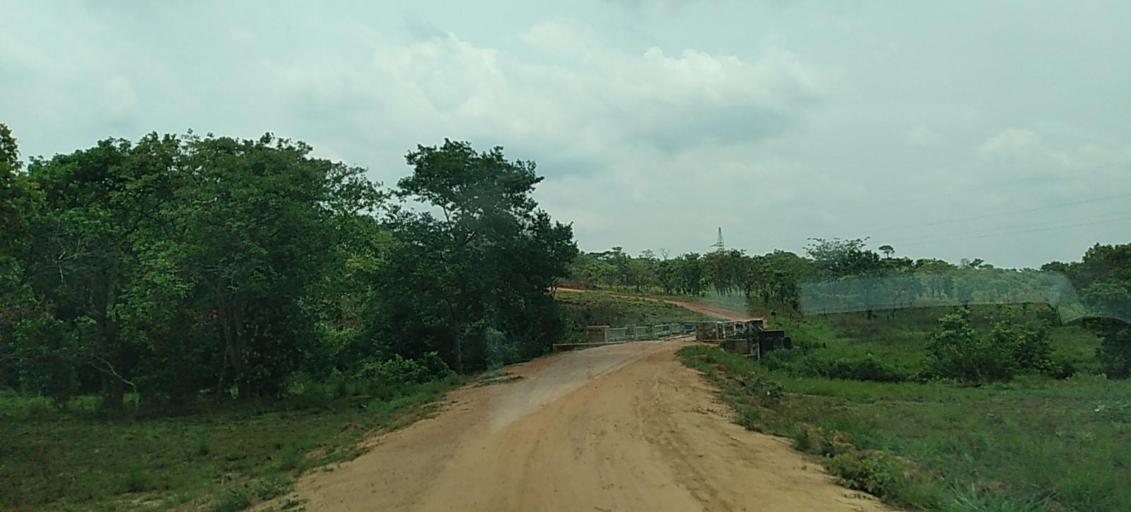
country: ZM
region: North-Western
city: Mwinilunga
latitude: -11.4584
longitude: 24.7598
